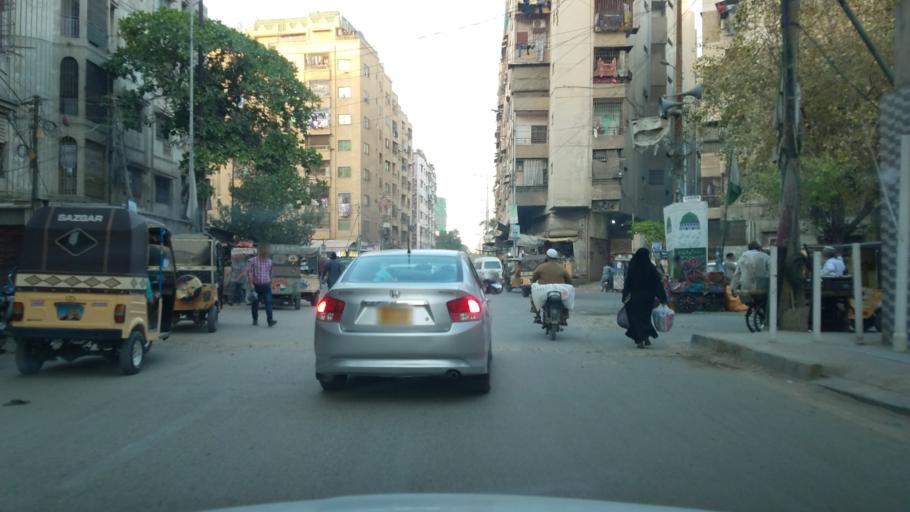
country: PK
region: Sindh
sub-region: Karachi District
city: Karachi
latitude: 24.8786
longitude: 67.0201
